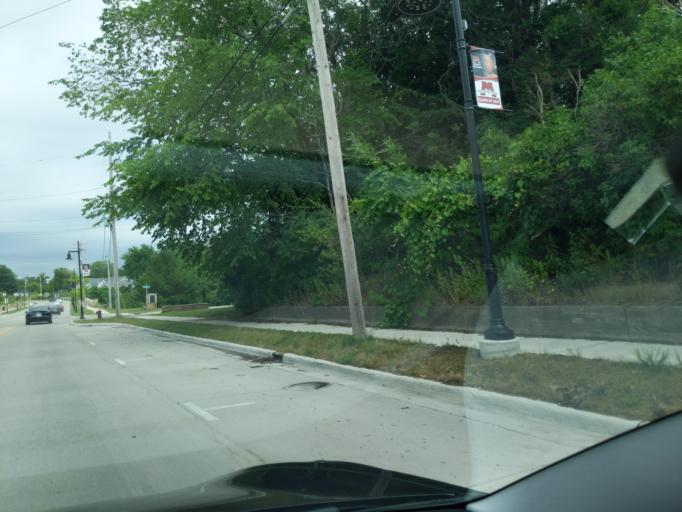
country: US
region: Michigan
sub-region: Muskegon County
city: Roosevelt Park
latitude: 43.2176
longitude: -86.2864
